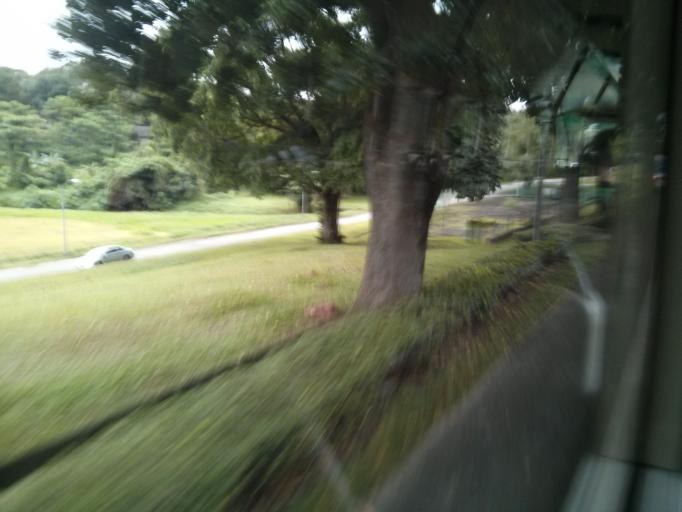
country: SG
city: Singapore
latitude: 1.2862
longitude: 103.7977
